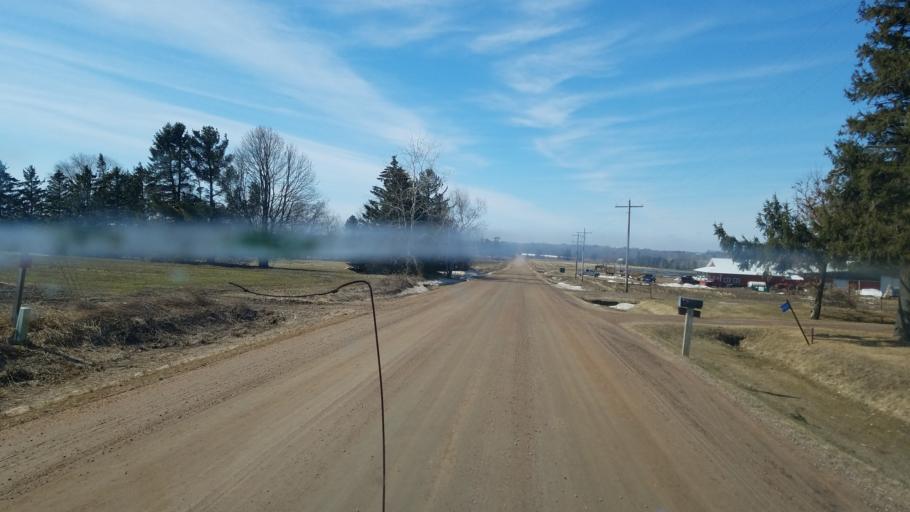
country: US
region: Wisconsin
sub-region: Clark County
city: Loyal
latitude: 44.6110
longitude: -90.4419
